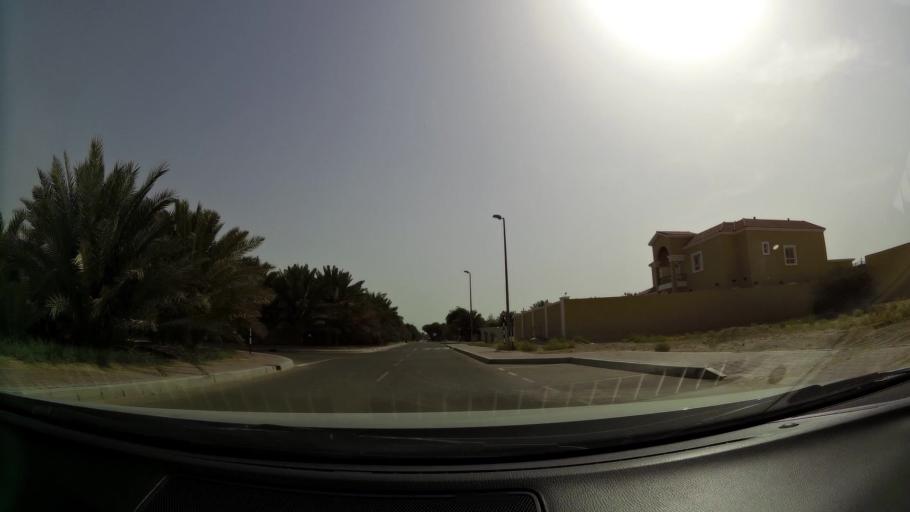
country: AE
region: Abu Dhabi
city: Al Ain
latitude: 24.1523
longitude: 55.7059
